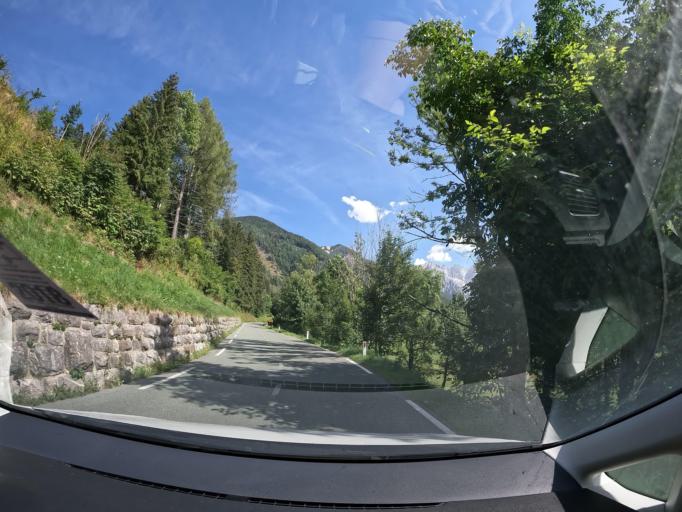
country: AT
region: Carinthia
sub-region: Politischer Bezirk Feldkirchen
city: Glanegg
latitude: 46.7166
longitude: 14.1607
